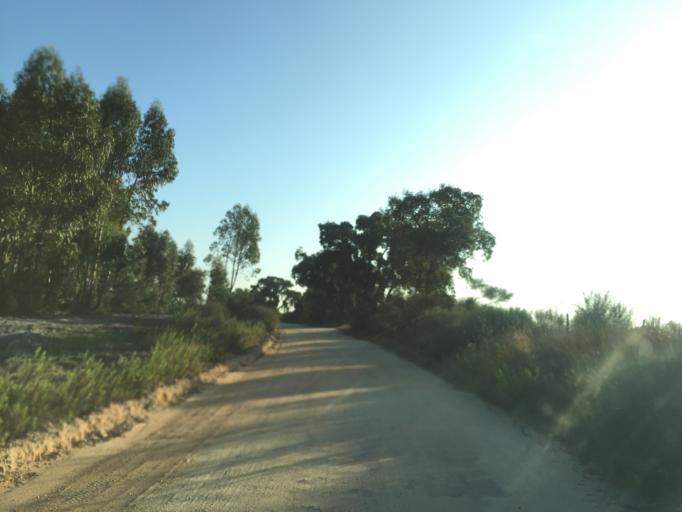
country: PT
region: Portalegre
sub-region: Ponte de Sor
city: Santo Andre
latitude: 39.1493
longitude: -8.3029
